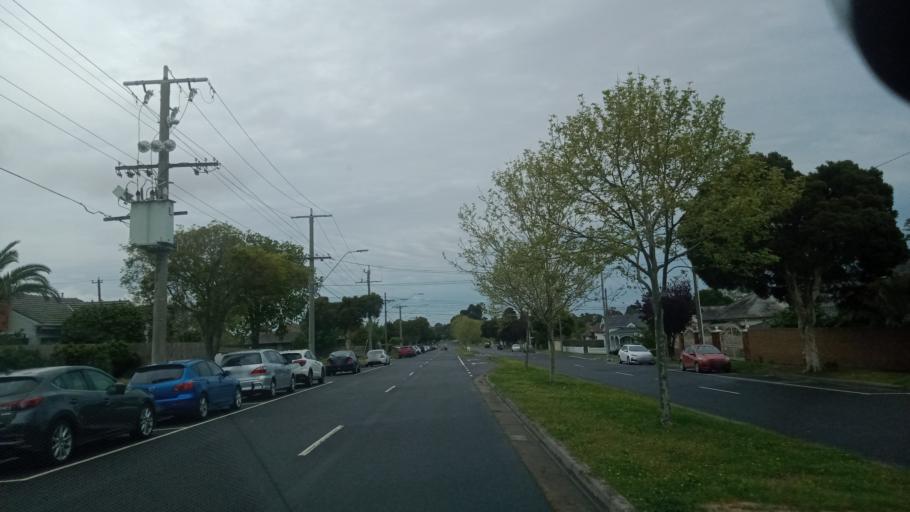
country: AU
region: Victoria
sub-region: Casey
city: Doveton
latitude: -37.9919
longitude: 145.2194
